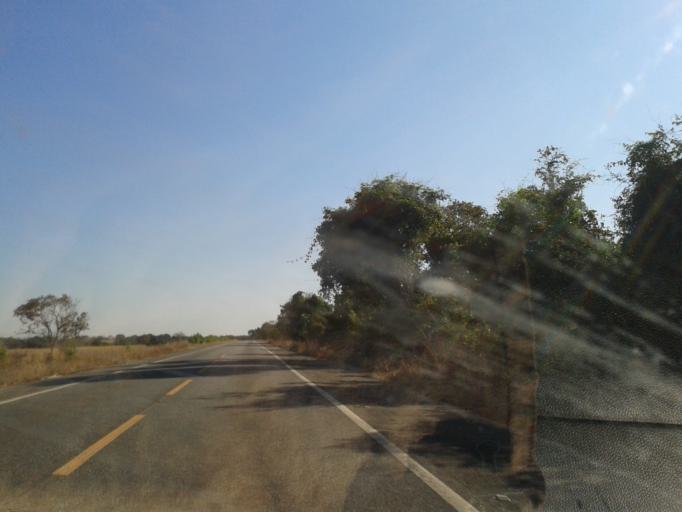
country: BR
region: Goias
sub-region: Mozarlandia
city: Mozarlandia
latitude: -14.9026
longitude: -50.5485
